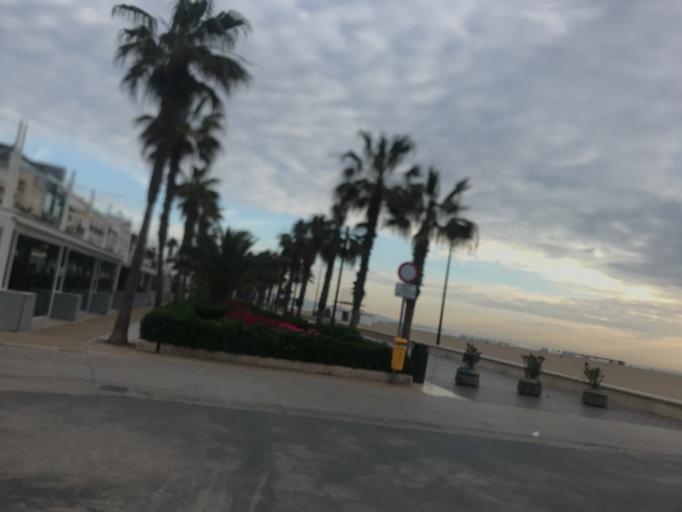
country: ES
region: Valencia
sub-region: Provincia de Valencia
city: Alboraya
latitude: 39.4629
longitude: -0.3228
